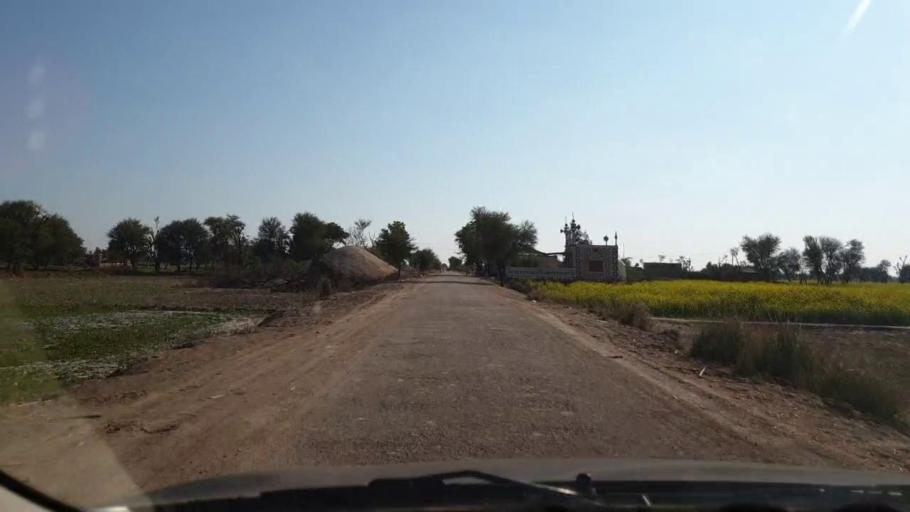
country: PK
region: Sindh
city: Sinjhoro
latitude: 25.9838
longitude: 68.8394
